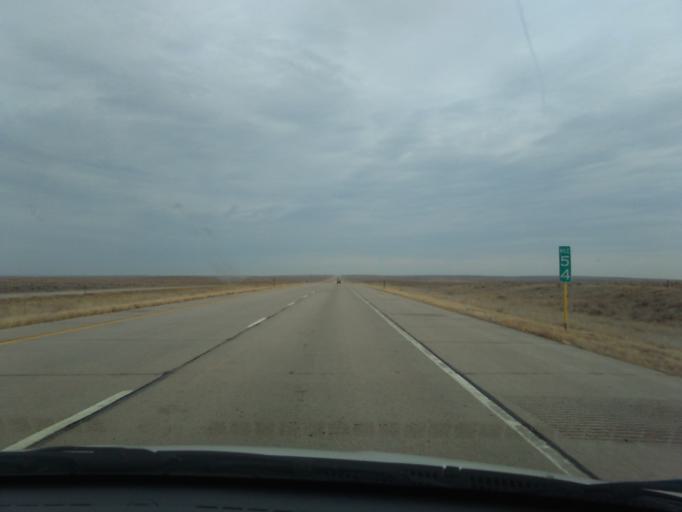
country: US
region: Colorado
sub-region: Weld County
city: Keenesburg
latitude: 40.1963
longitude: -104.2705
